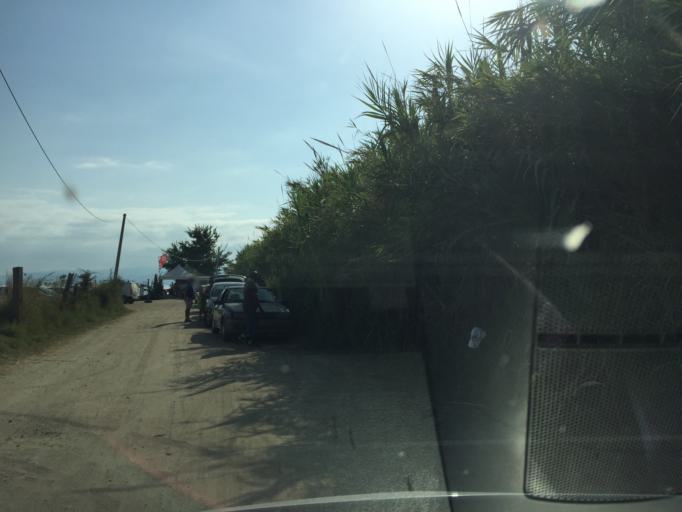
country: IT
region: Calabria
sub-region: Provincia di Vibo-Valentia
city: Briatico
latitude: 38.7207
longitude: 16.0586
